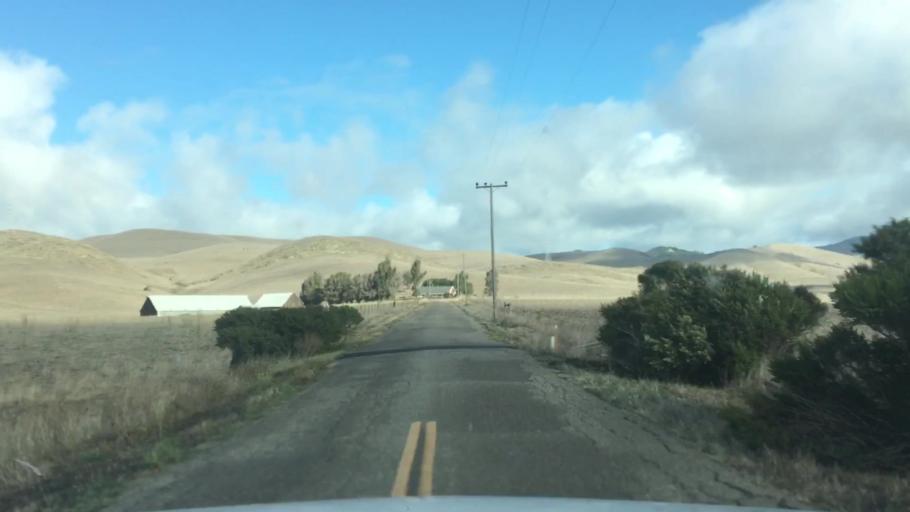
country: US
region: California
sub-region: San Luis Obispo County
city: Morro Bay
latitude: 35.3672
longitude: -120.8040
